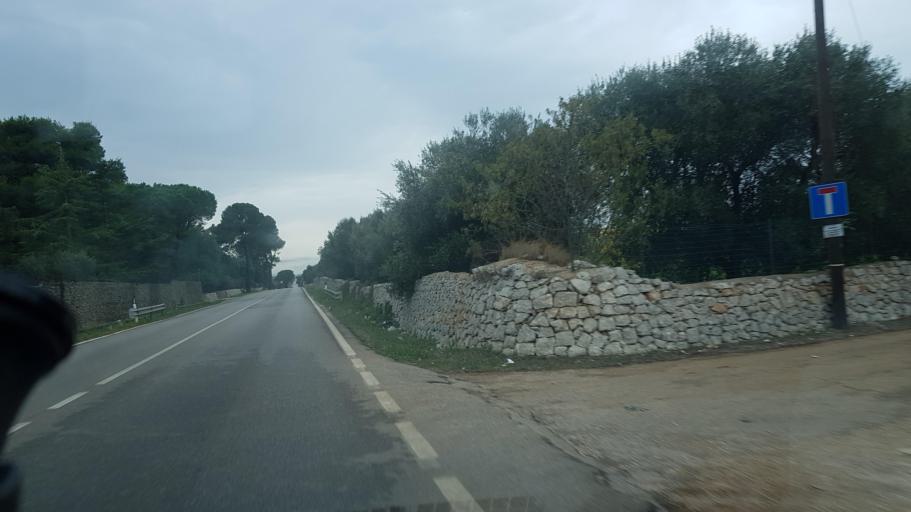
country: IT
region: Apulia
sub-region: Provincia di Brindisi
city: Carovigno
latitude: 40.7107
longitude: 17.6362
